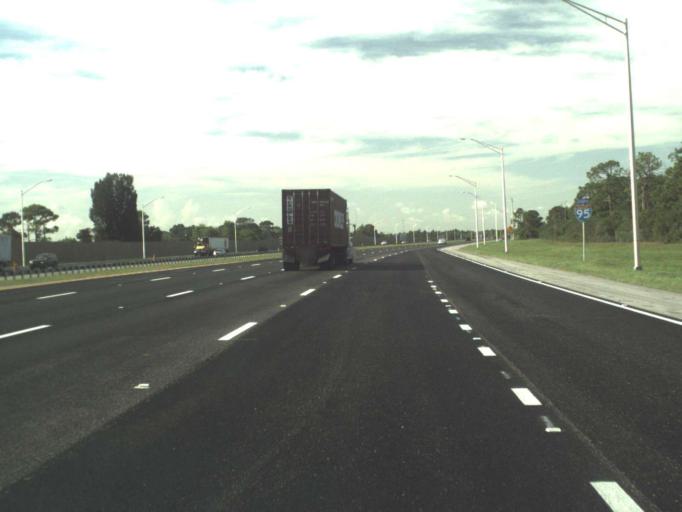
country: US
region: Florida
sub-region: Indian River County
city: West Vero Corridor
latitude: 27.6333
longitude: -80.5161
